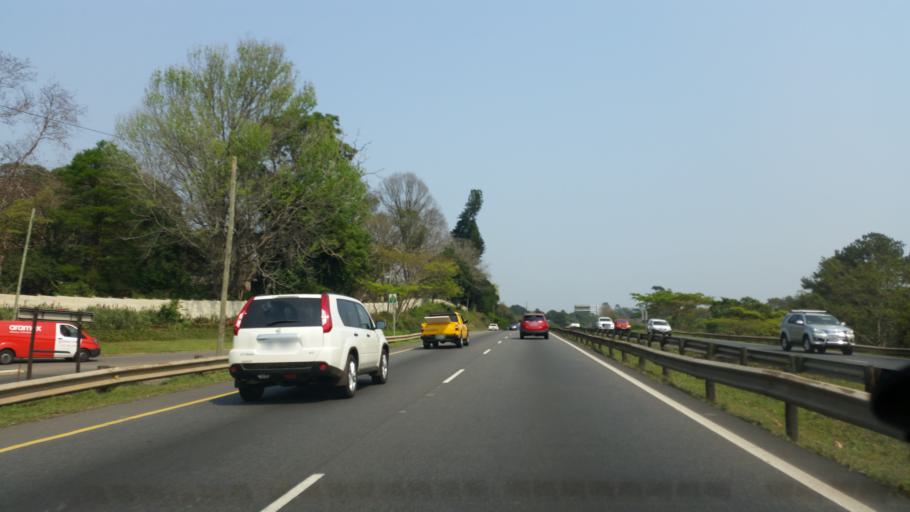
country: ZA
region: KwaZulu-Natal
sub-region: eThekwini Metropolitan Municipality
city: Mpumalanga
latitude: -29.7931
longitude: 30.8179
